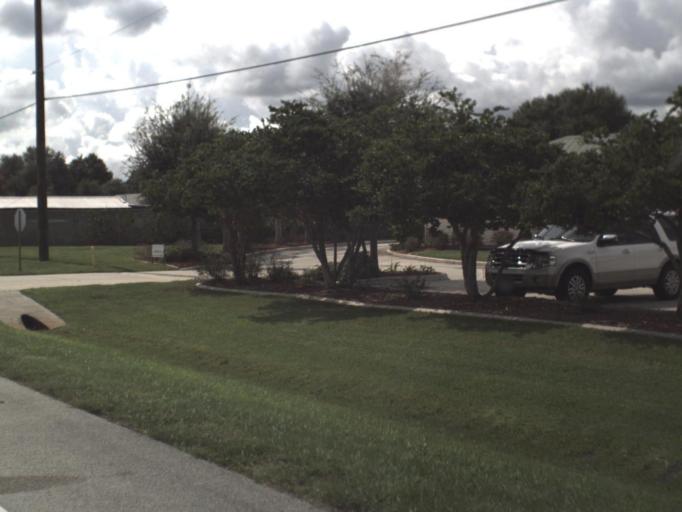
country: US
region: Florida
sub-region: DeSoto County
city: Arcadia
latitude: 27.2122
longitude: -81.9117
